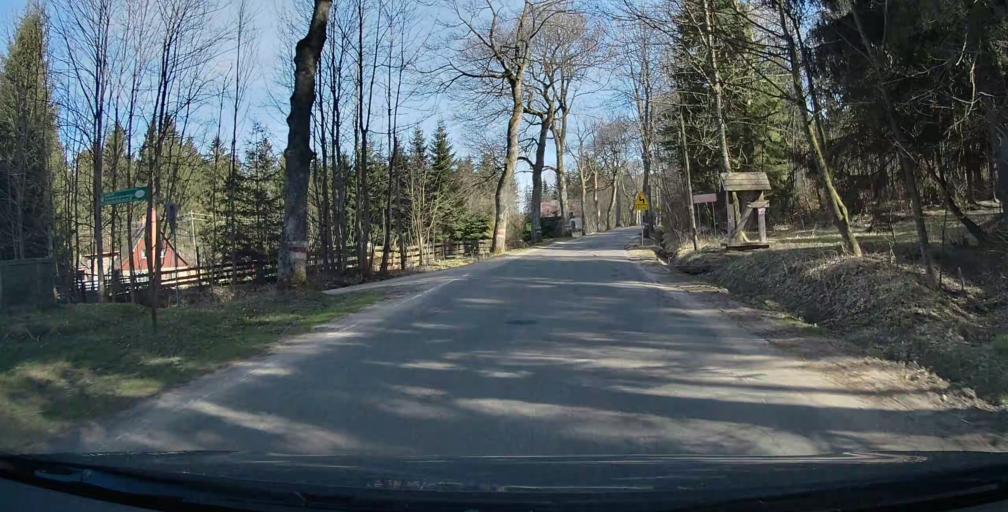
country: PL
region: Lower Silesian Voivodeship
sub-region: Powiat klodzki
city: Radkow
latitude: 50.4694
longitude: 16.3420
